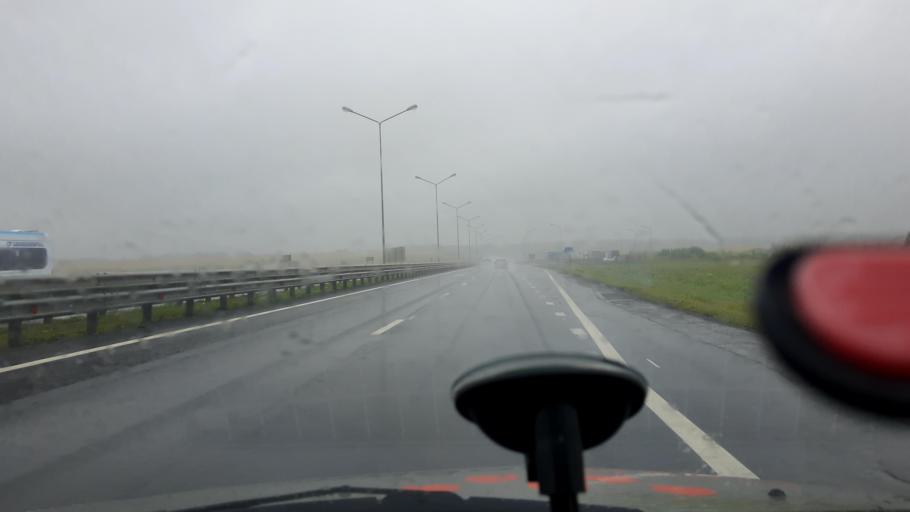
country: RU
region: Bashkortostan
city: Kushnarenkovo
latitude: 55.0727
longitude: 55.2879
